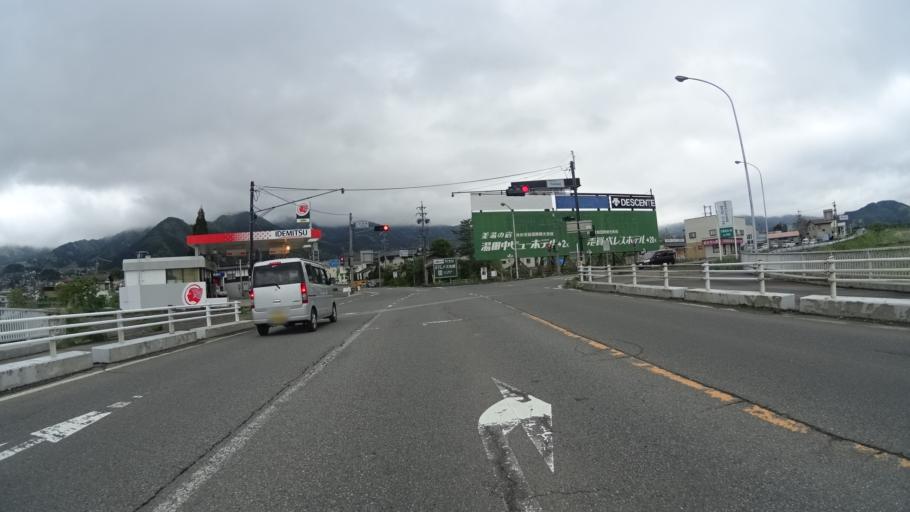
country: JP
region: Nagano
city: Nakano
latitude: 36.7581
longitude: 138.3979
